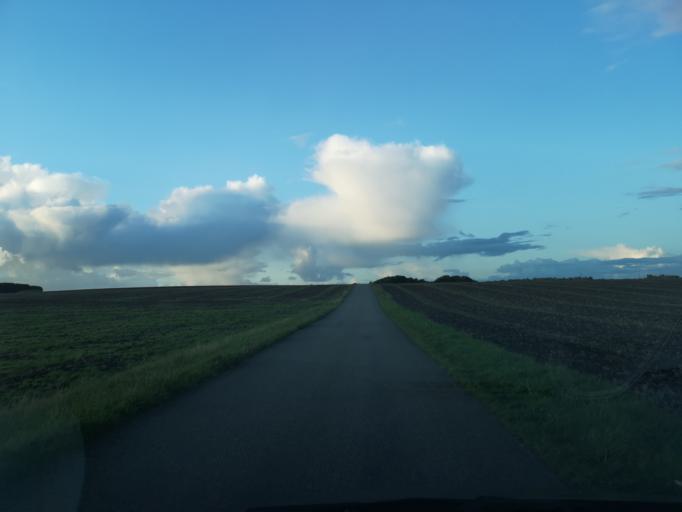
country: DK
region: Central Jutland
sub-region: Ringkobing-Skjern Kommune
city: Videbaek
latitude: 56.0366
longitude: 8.5771
